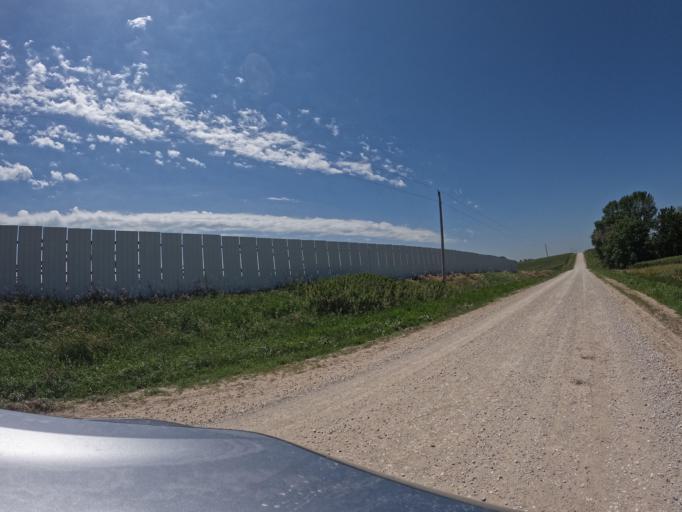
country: US
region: Iowa
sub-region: Poweshiek County
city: Montezuma
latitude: 41.4666
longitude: -92.3682
